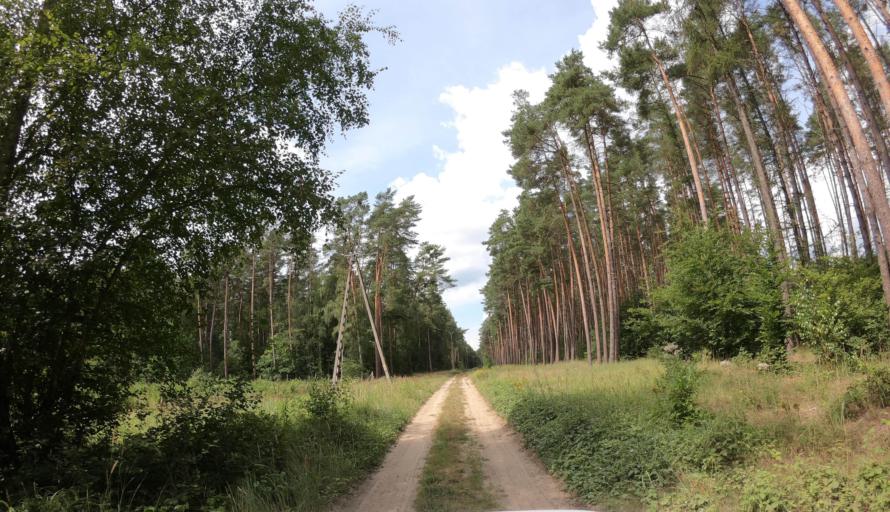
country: PL
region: West Pomeranian Voivodeship
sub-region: Powiat stargardzki
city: Kobylanka
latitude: 53.3286
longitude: 14.8157
